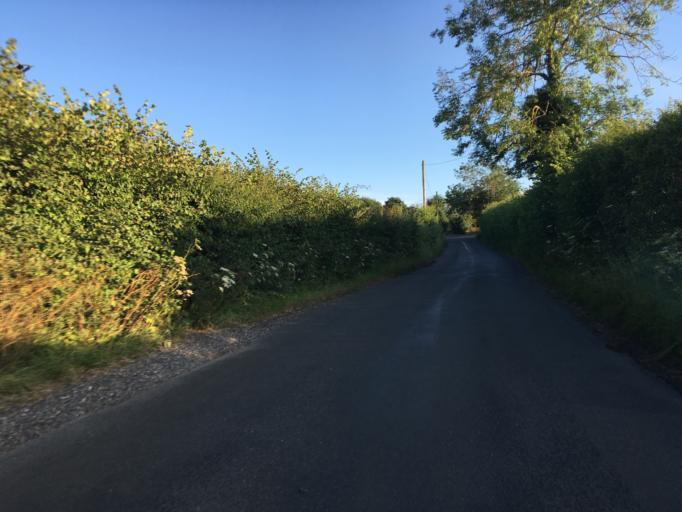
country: GB
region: England
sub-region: Hampshire
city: Tadley
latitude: 51.4180
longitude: -1.1627
